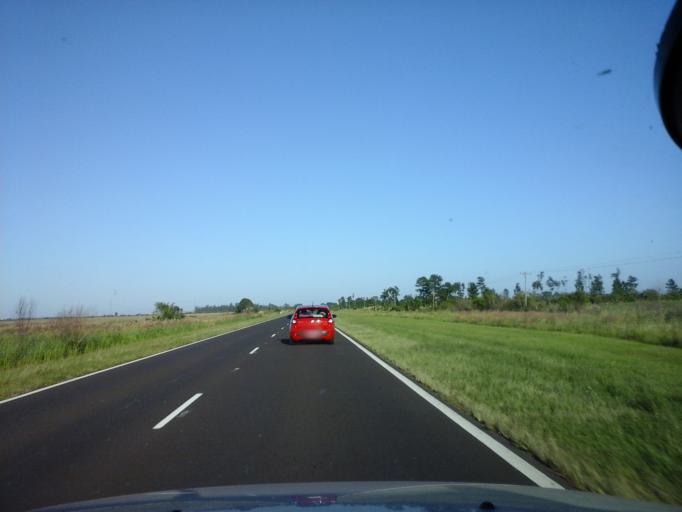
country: AR
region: Corrientes
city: Ita Ibate
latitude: -27.4955
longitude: -57.2644
